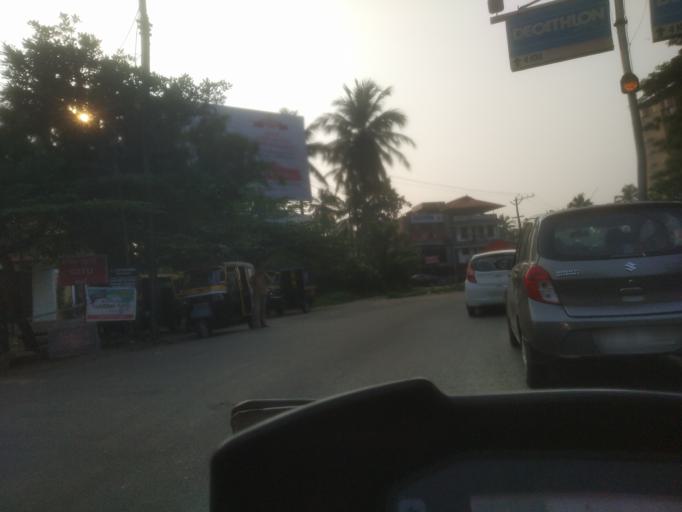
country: IN
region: Kerala
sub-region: Ernakulam
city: Cochin
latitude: 9.9385
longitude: 76.3271
